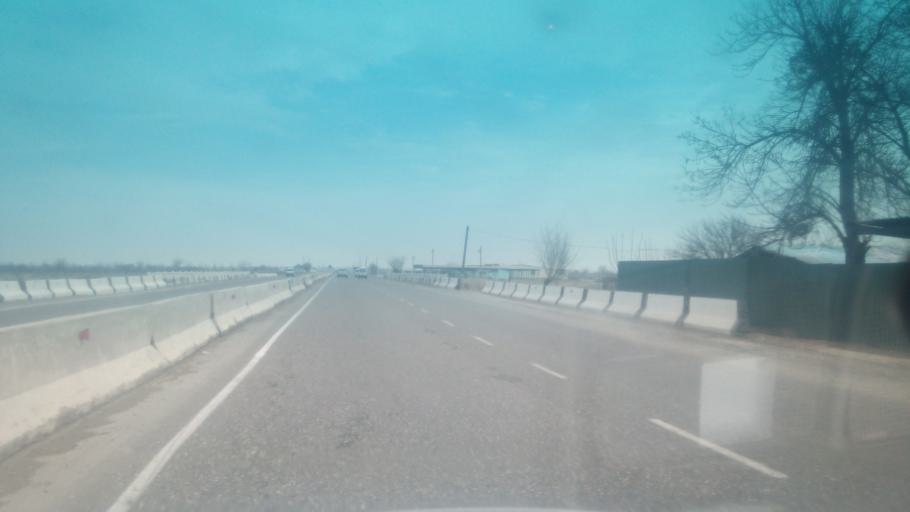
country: KZ
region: Ongtustik Qazaqstan
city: Myrzakent
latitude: 40.5023
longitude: 68.5322
